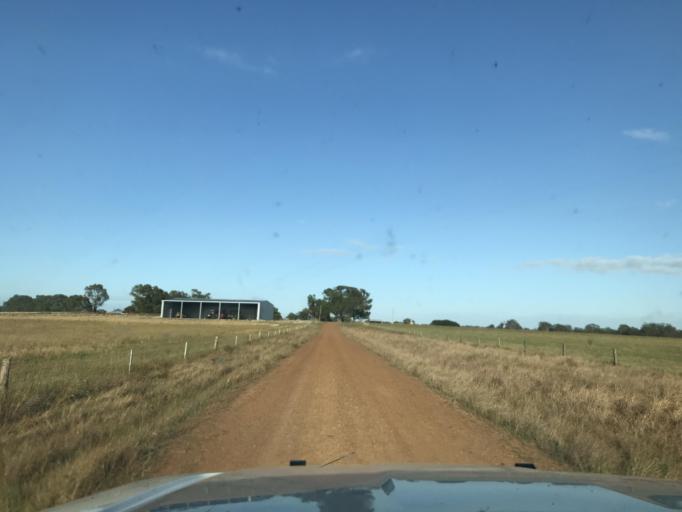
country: AU
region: South Australia
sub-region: Naracoorte and Lucindale
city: Naracoorte
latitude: -36.9551
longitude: 141.3617
